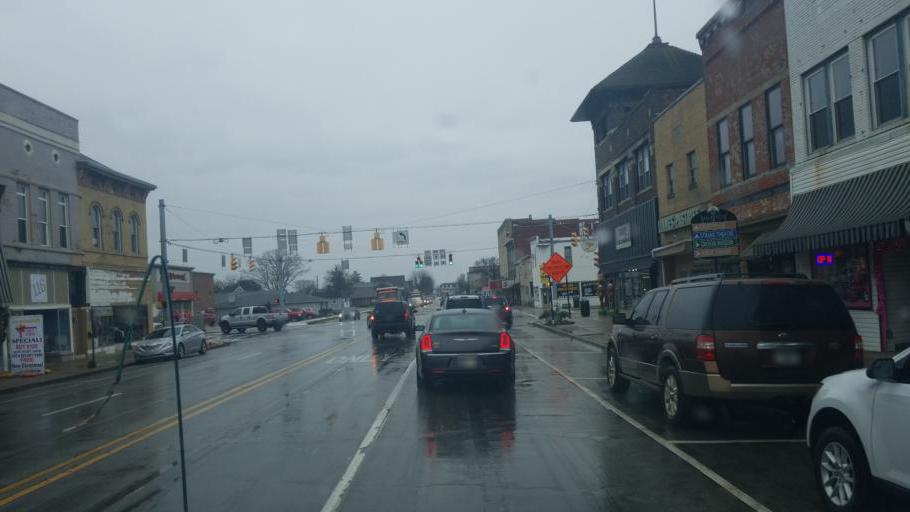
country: US
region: Indiana
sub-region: Shelby County
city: Shelbyville
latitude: 39.5235
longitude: -85.7771
